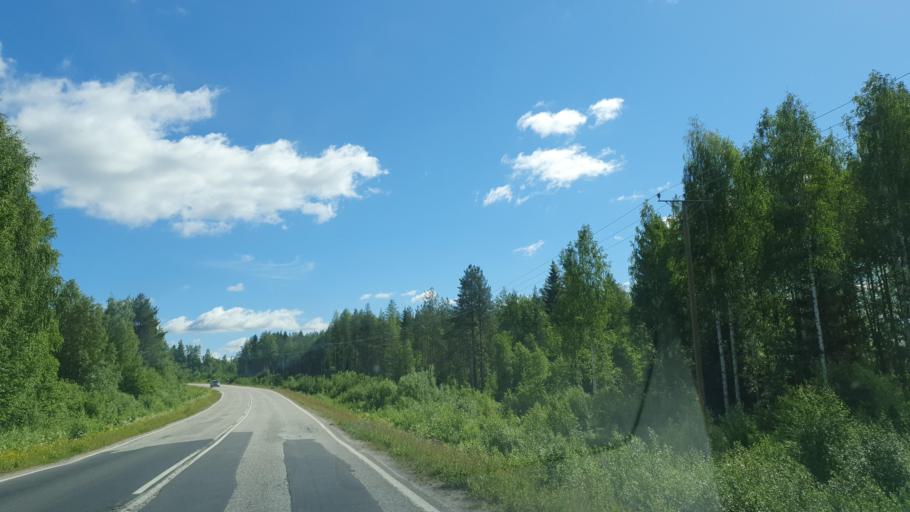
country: FI
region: Kainuu
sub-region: Kehys-Kainuu
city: Kuhmo
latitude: 64.1438
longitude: 29.6221
